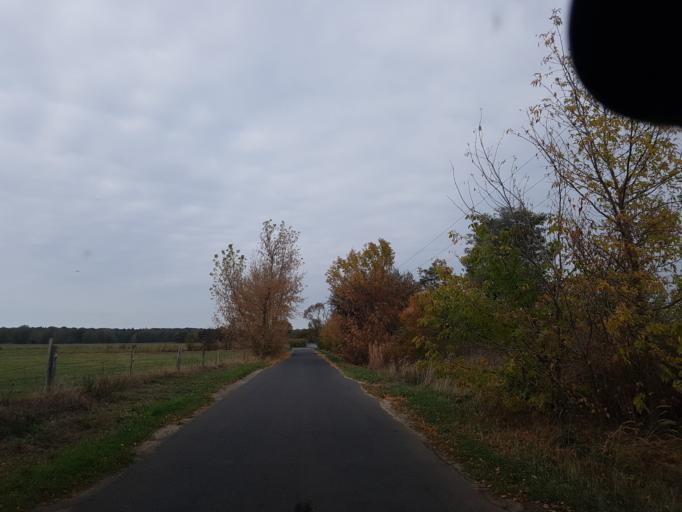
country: DE
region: Brandenburg
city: Finsterwalde
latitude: 51.6148
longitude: 13.6946
